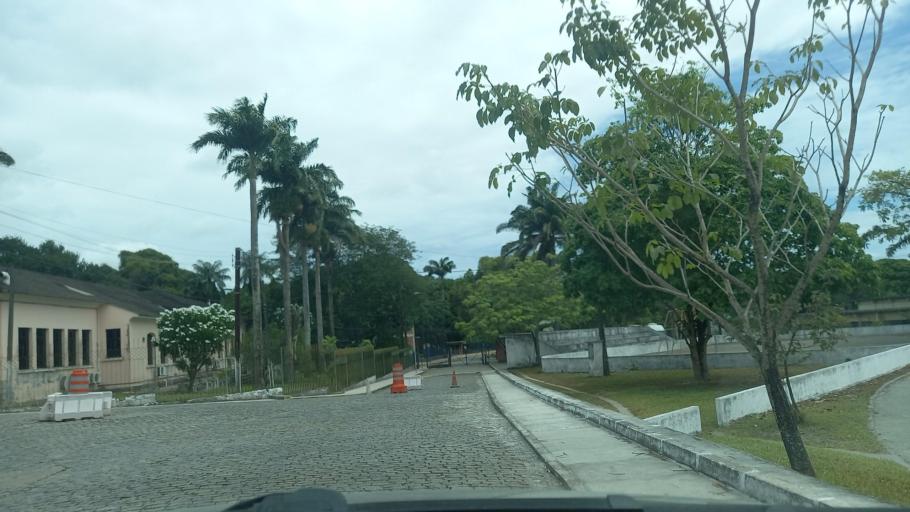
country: BR
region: Pernambuco
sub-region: Sao Lourenco Da Mata
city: Sao Lourenco da Mata
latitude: -8.0141
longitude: -34.9498
